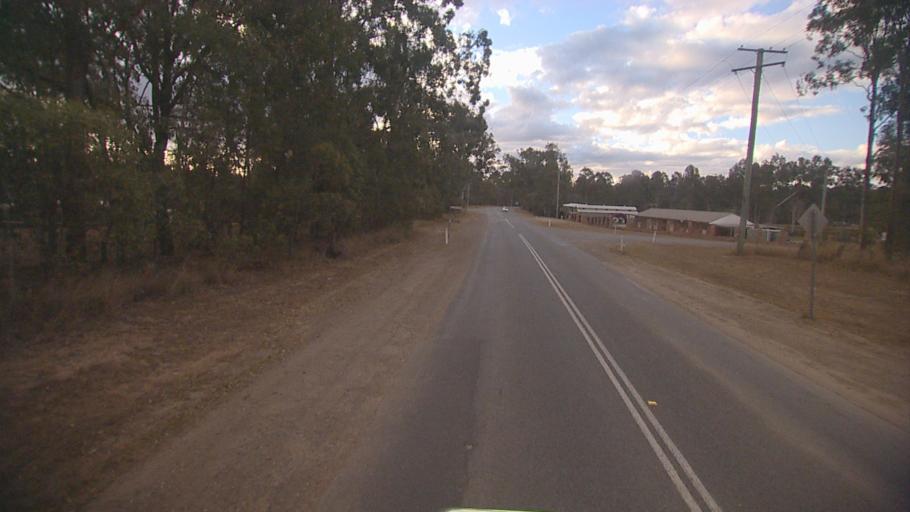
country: AU
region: Queensland
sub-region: Logan
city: Cedar Vale
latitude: -27.8552
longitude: 153.0531
